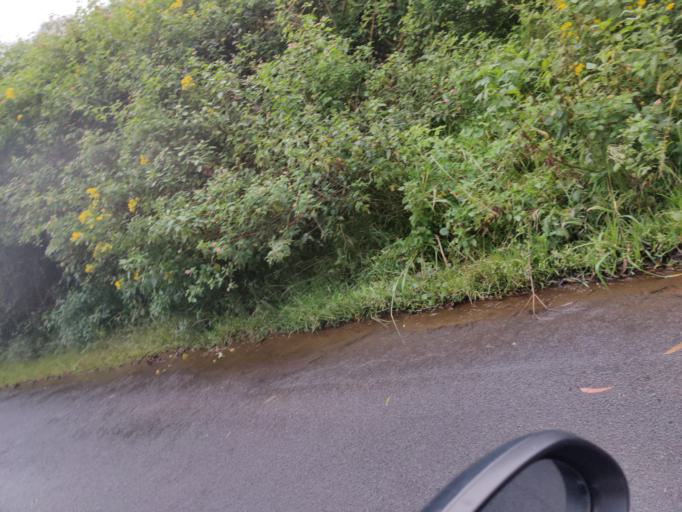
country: AU
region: New South Wales
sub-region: Pittwater
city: Ingleside
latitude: -33.6748
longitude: 151.2556
